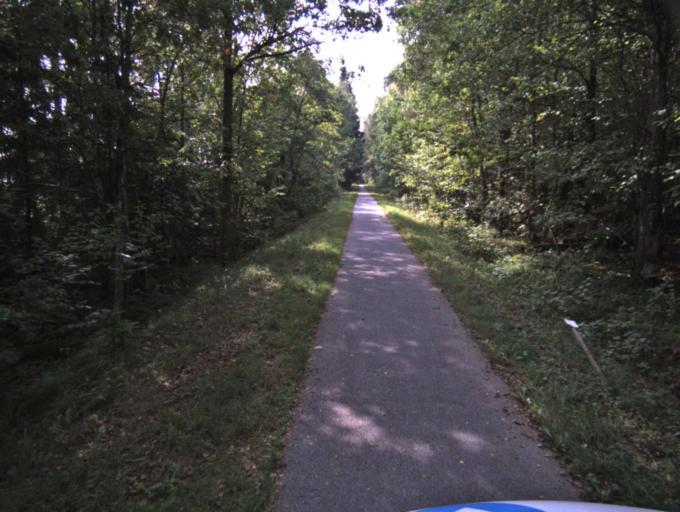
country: SE
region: Vaestra Goetaland
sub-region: Tranemo Kommun
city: Limmared
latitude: 57.6277
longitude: 13.3487
